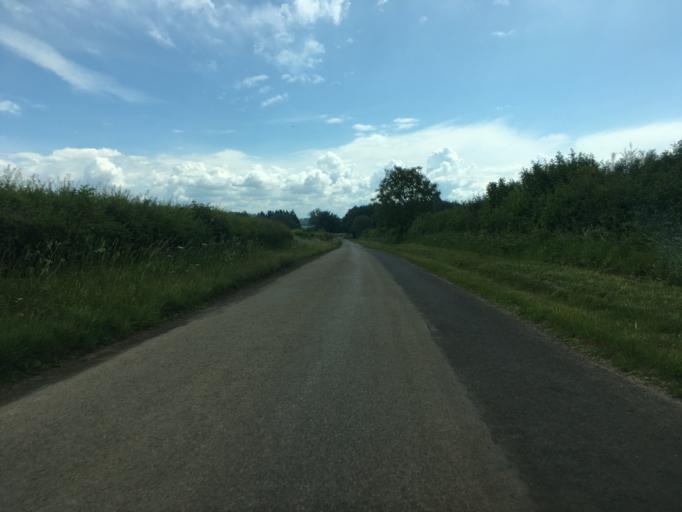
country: GB
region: England
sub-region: Gloucestershire
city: Coates
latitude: 51.7405
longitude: -2.0570
